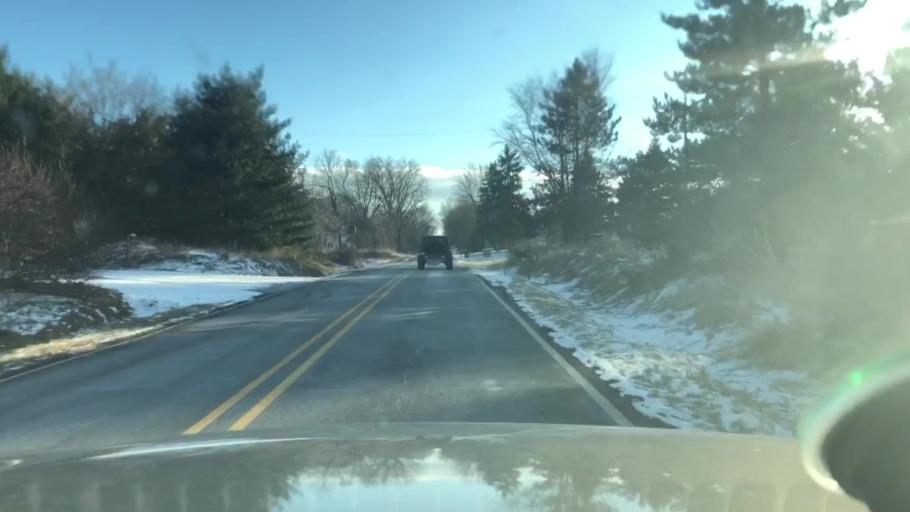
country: US
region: Michigan
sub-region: Jackson County
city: Vandercook Lake
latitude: 42.1375
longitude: -84.4517
